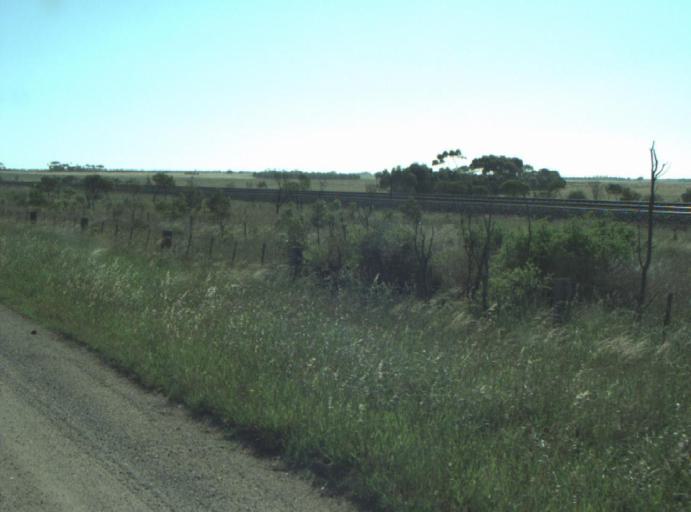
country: AU
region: Victoria
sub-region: Greater Geelong
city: Lara
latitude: -37.9966
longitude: 144.4470
